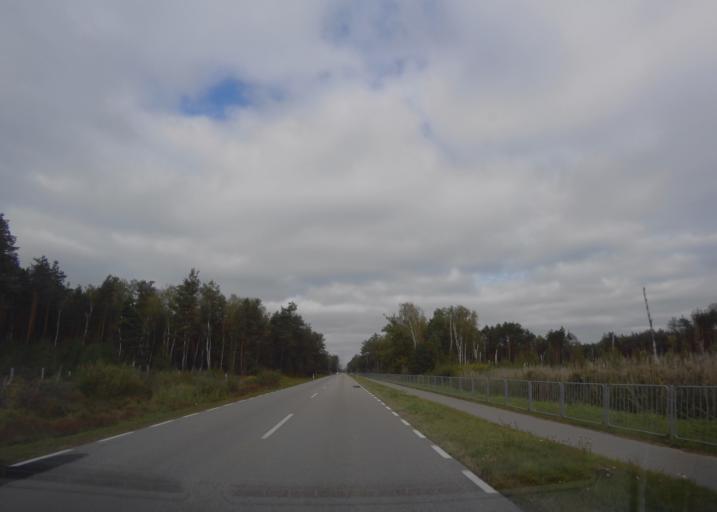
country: PL
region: Lublin Voivodeship
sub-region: Powiat wlodawski
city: Wlodawa
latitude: 51.4828
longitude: 23.5158
